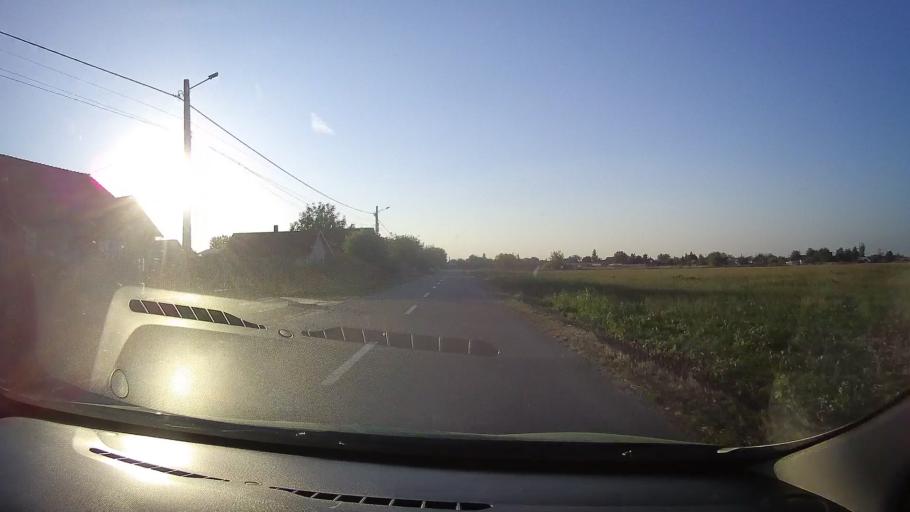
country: RO
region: Bihor
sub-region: Comuna Biharea
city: Biharea
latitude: 47.1637
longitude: 21.9534
